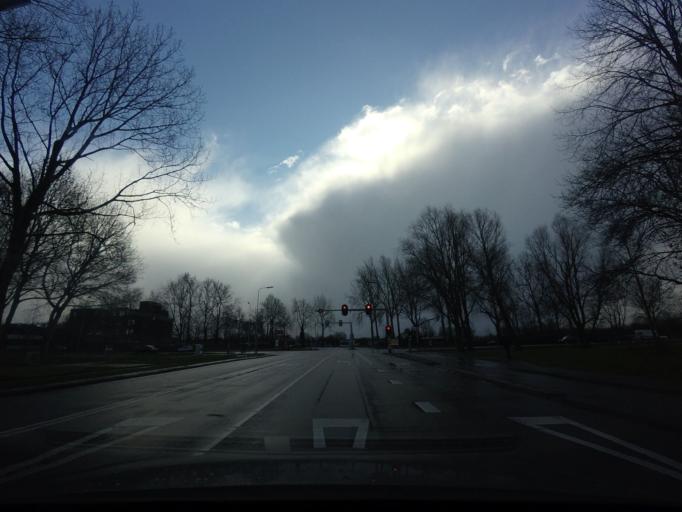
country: NL
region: Groningen
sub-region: Gemeente Groningen
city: Groningen
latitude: 53.2151
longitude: 6.5306
